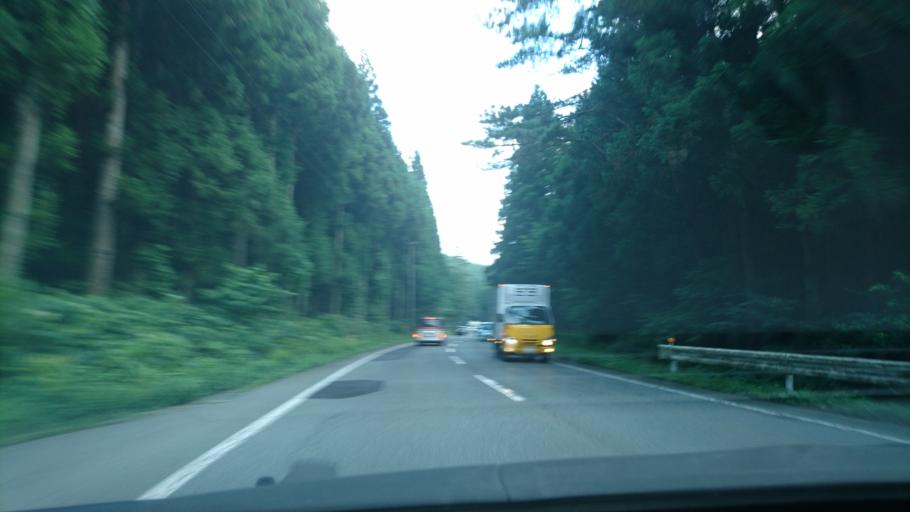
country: JP
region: Iwate
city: Mizusawa
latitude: 39.0449
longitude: 141.2358
